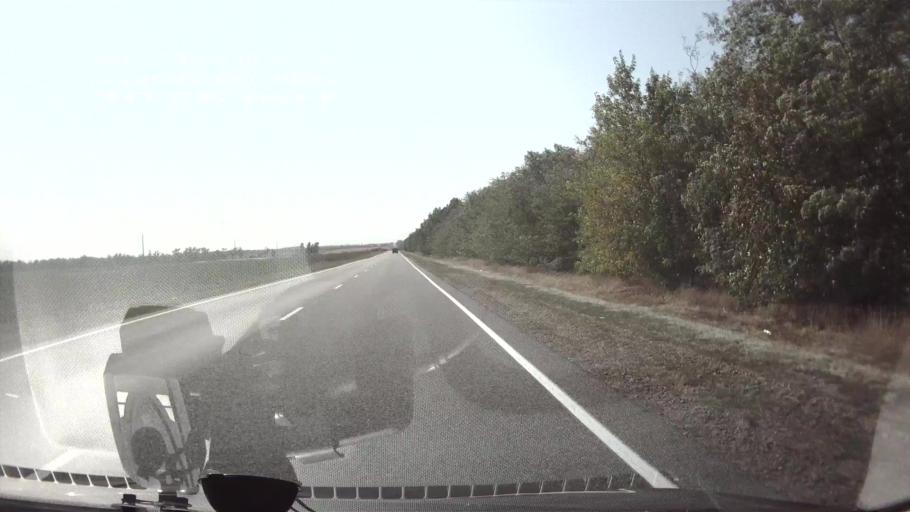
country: RU
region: Krasnodarskiy
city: Novopokrovskaya
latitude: 45.8600
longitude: 40.7206
